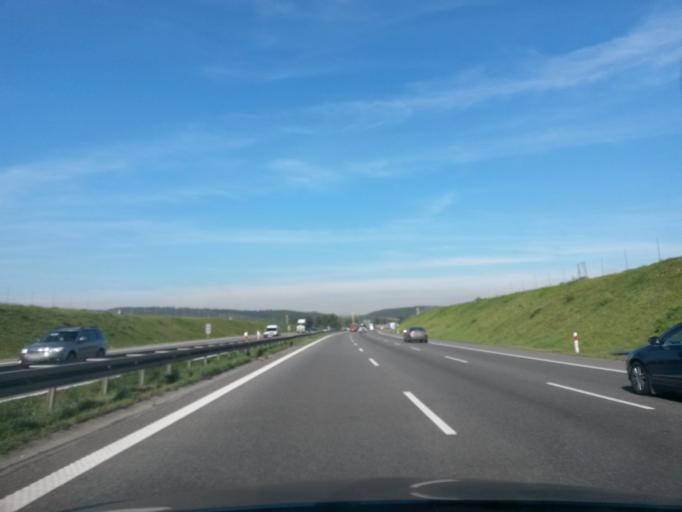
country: PL
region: Lesser Poland Voivodeship
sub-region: Powiat krakowski
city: Balice
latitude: 50.0787
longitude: 19.8087
